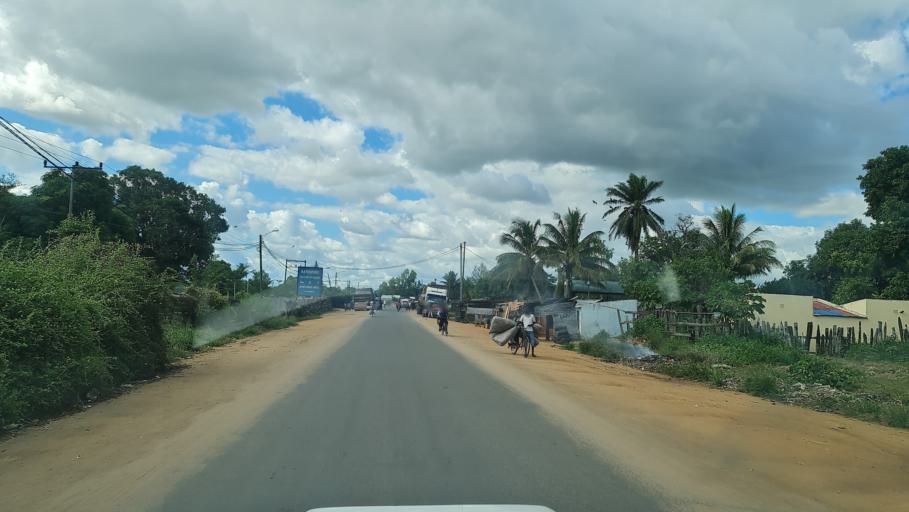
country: MZ
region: Zambezia
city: Quelimane
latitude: -17.5968
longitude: 36.8114
